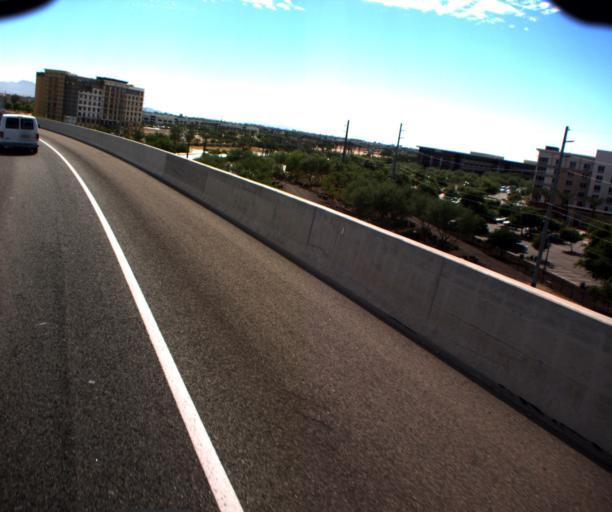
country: US
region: Arizona
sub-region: Maricopa County
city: Chandler
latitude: 33.2915
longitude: -111.8931
